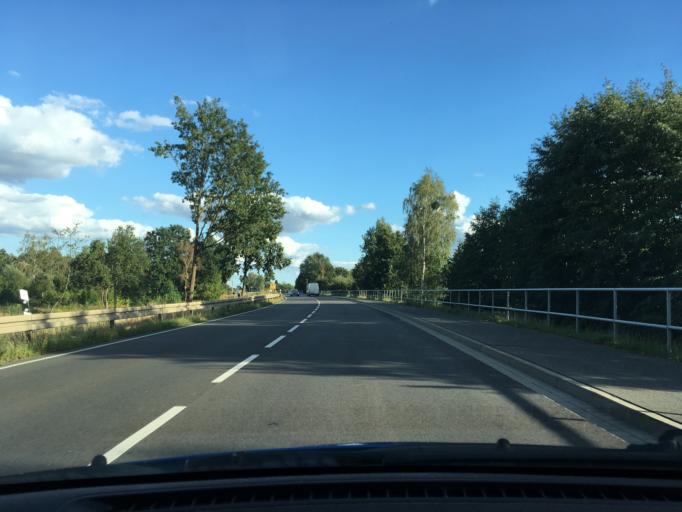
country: DE
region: Mecklenburg-Vorpommern
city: Grabow
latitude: 53.2782
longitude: 11.5555
